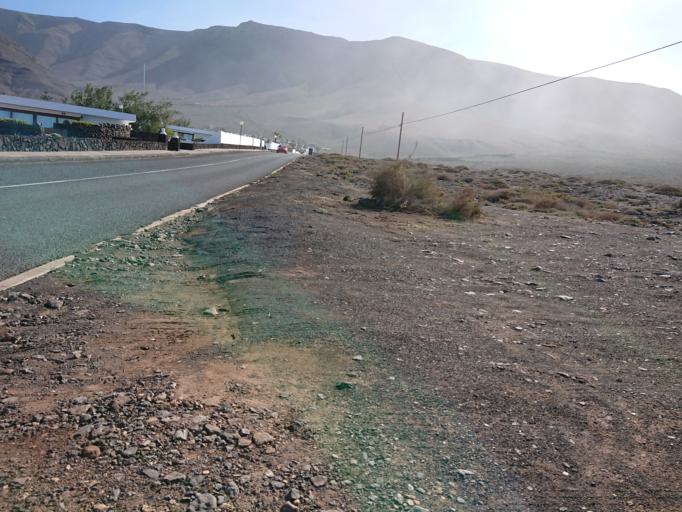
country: ES
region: Canary Islands
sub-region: Provincia de Las Palmas
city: Teguise
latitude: 29.1138
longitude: -13.5506
